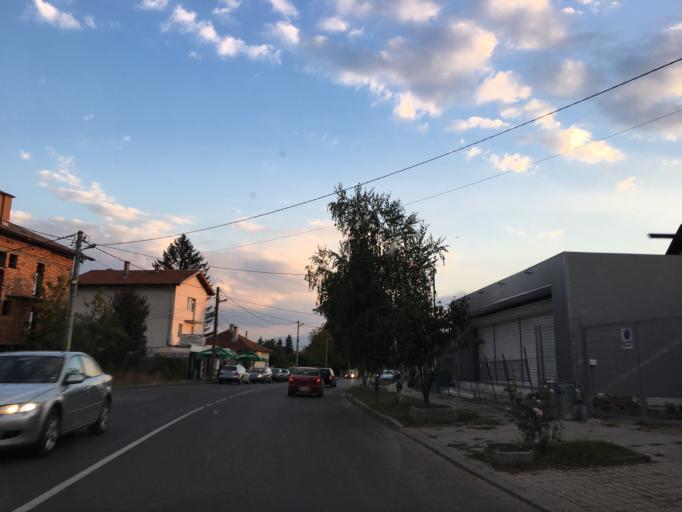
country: BG
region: Sofia-Capital
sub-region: Stolichna Obshtina
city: Sofia
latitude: 42.8191
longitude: 23.3536
